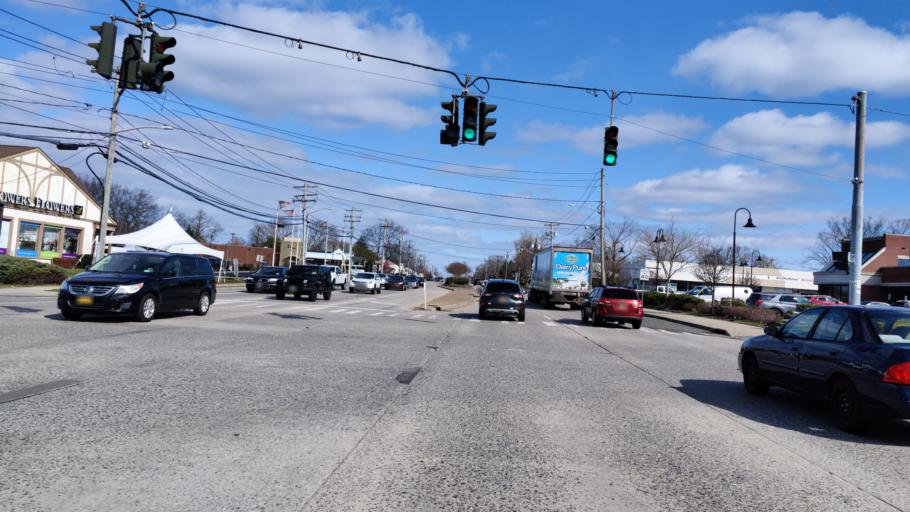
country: US
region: New York
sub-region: Suffolk County
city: Deer Park
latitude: 40.7424
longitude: -73.3218
